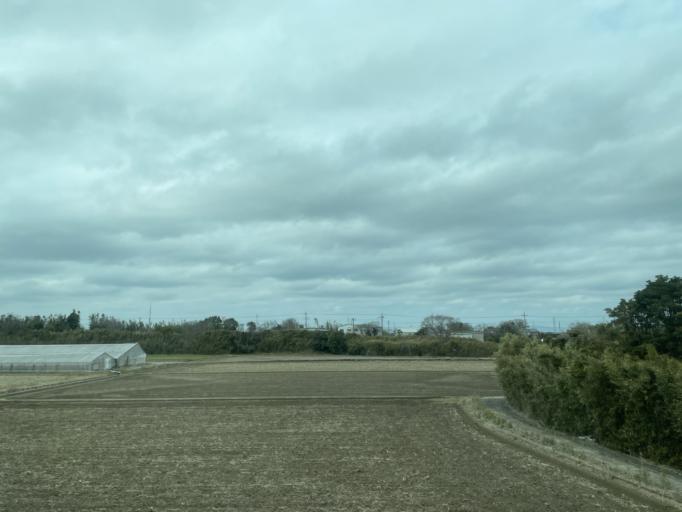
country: JP
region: Ibaraki
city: Ryugasaki
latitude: 35.8358
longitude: 140.2127
